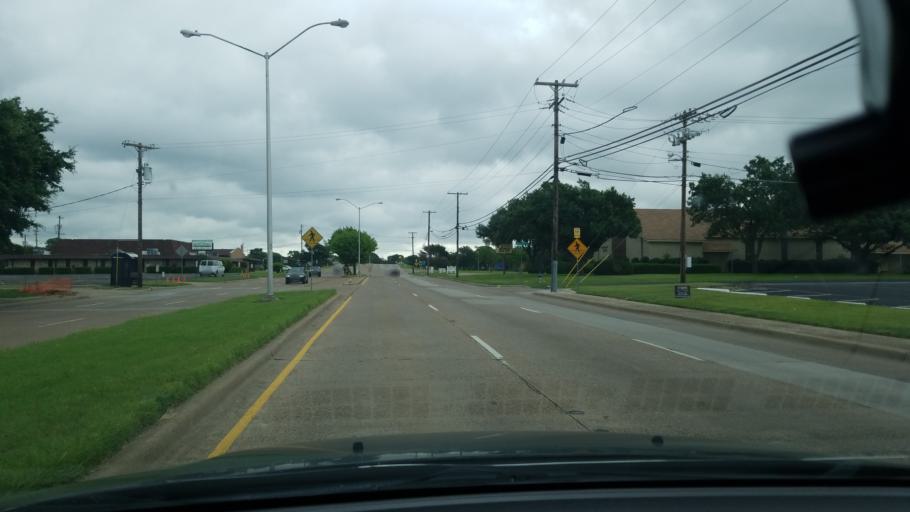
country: US
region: Texas
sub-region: Dallas County
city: Highland Park
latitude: 32.8157
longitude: -96.6928
